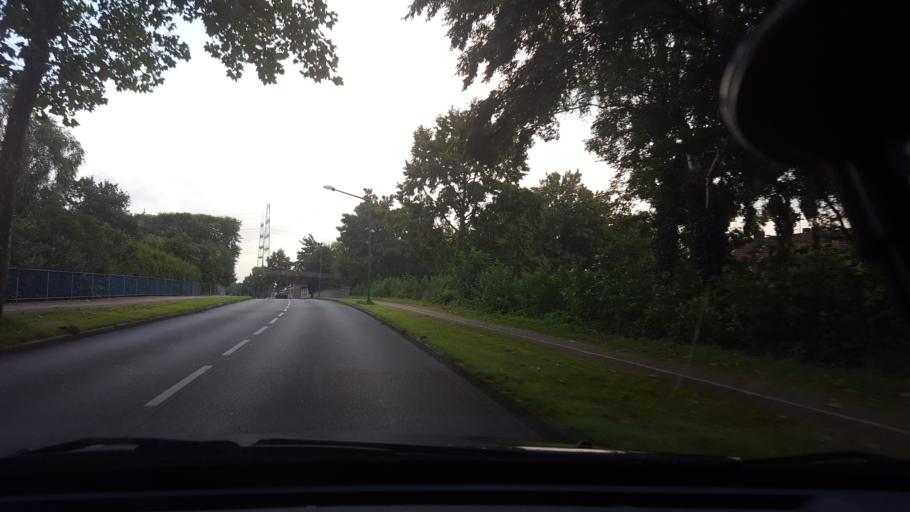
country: DE
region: North Rhine-Westphalia
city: Herten
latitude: 51.6023
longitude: 7.0974
